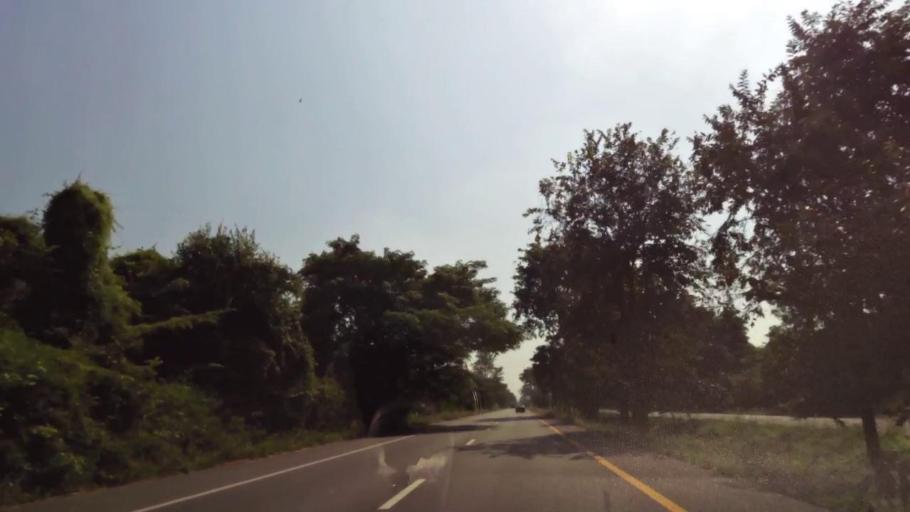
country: TH
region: Nakhon Sawan
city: Banphot Phisai
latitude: 16.0023
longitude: 100.1161
